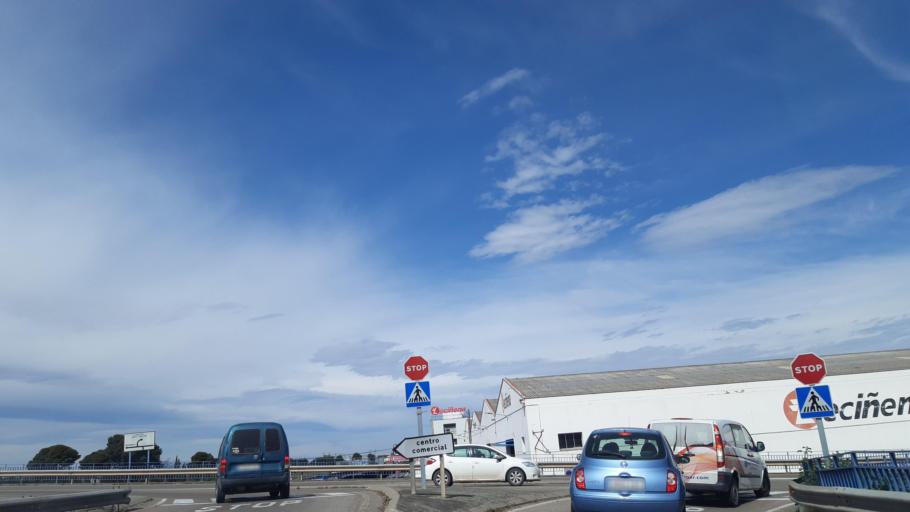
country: ES
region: Aragon
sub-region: Provincia de Zaragoza
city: Utebo
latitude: 41.7046
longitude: -1.0041
